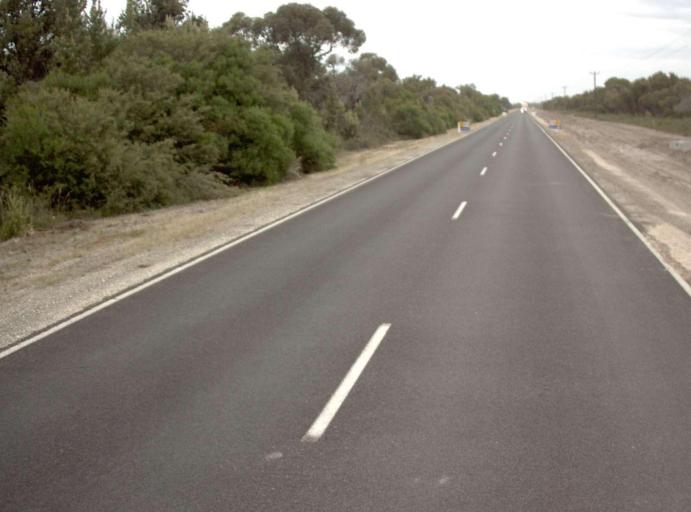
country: AU
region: Victoria
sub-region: East Gippsland
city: Bairnsdale
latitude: -38.0792
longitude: 147.5356
